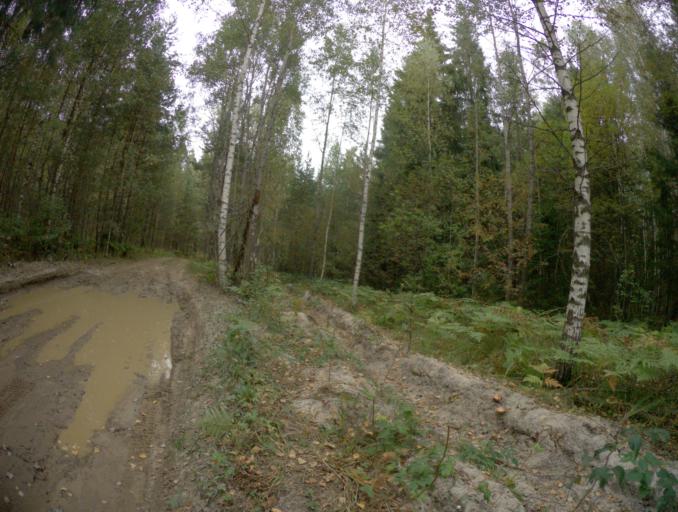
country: RU
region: Vladimir
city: Raduzhnyy
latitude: 55.8937
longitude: 40.1904
